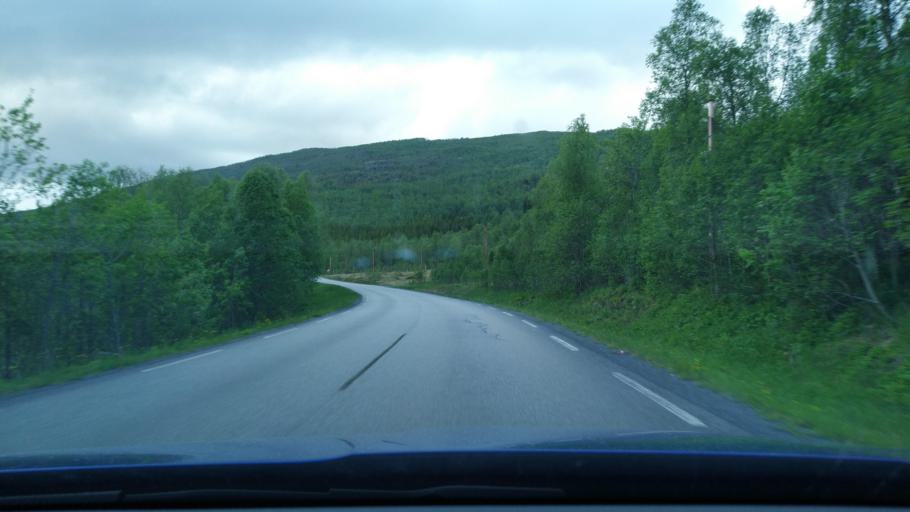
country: NO
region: Troms
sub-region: Dyroy
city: Brostadbotn
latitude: 69.0514
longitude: 17.8226
